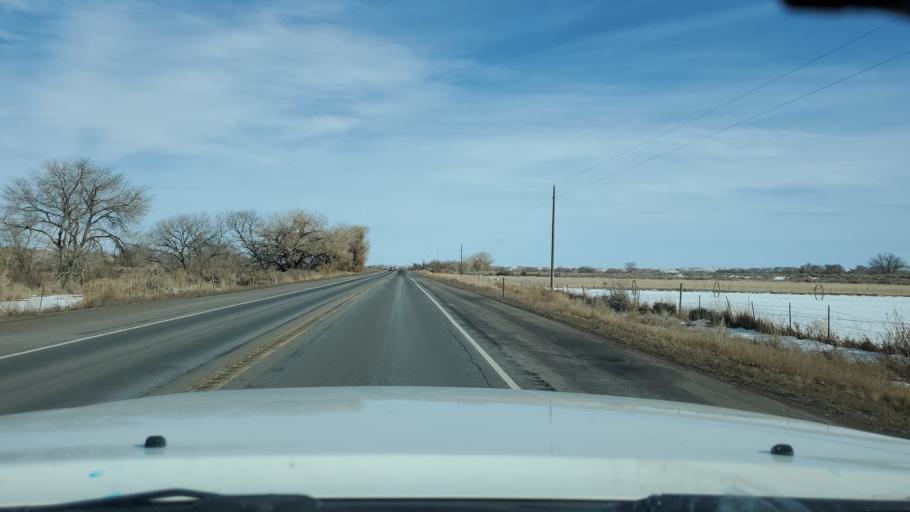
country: US
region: Utah
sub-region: Duchesne County
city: Duchesne
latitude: 40.1553
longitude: -110.2054
